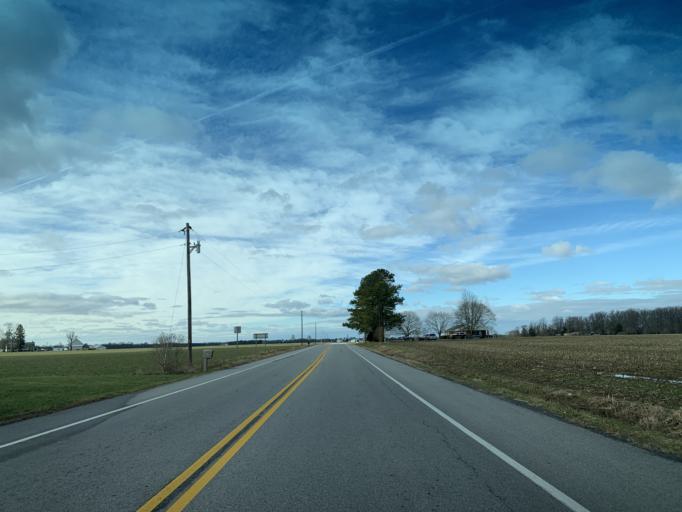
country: US
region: Maryland
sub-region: Queen Anne's County
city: Kingstown
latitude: 39.3205
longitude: -75.9777
